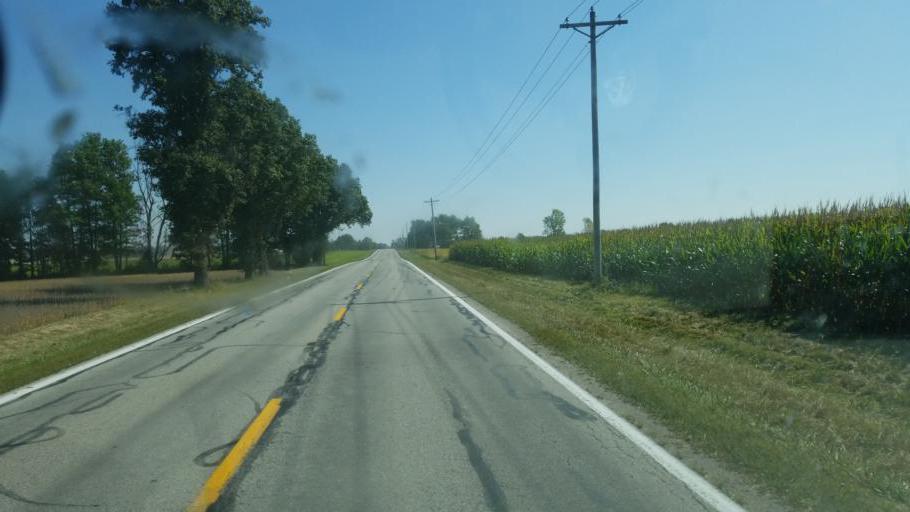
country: US
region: Ohio
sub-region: Wyandot County
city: Upper Sandusky
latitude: 40.6435
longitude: -83.3728
